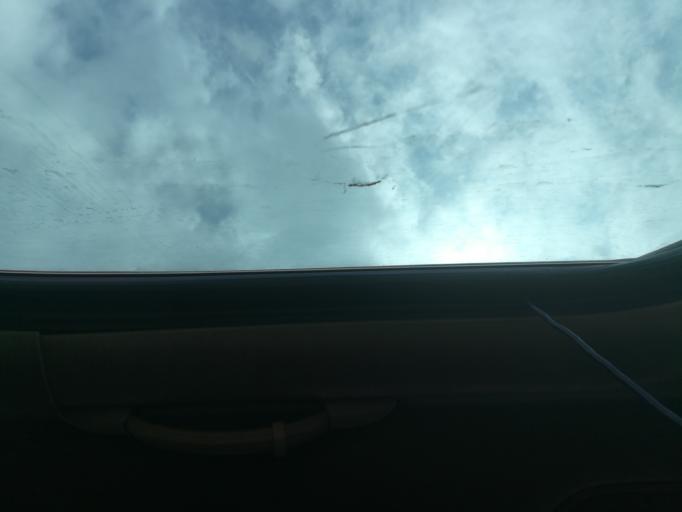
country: NG
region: Lagos
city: Ikoyi
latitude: 6.4092
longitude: 3.4157
